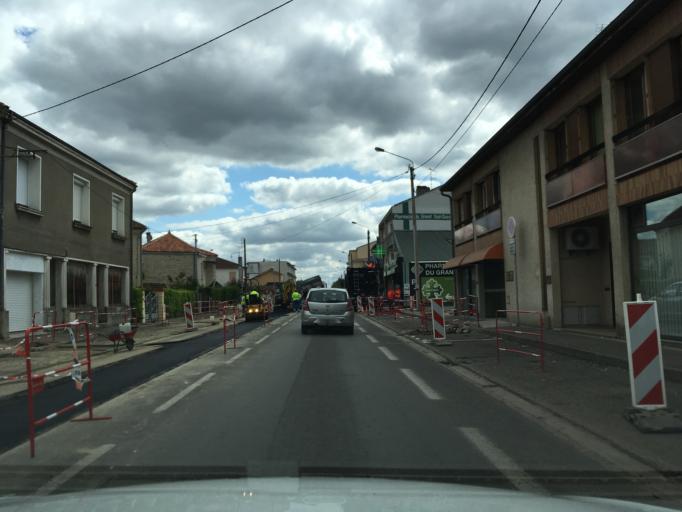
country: FR
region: Aquitaine
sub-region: Departement du Lot-et-Garonne
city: Agen
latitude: 44.1973
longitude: 0.6271
